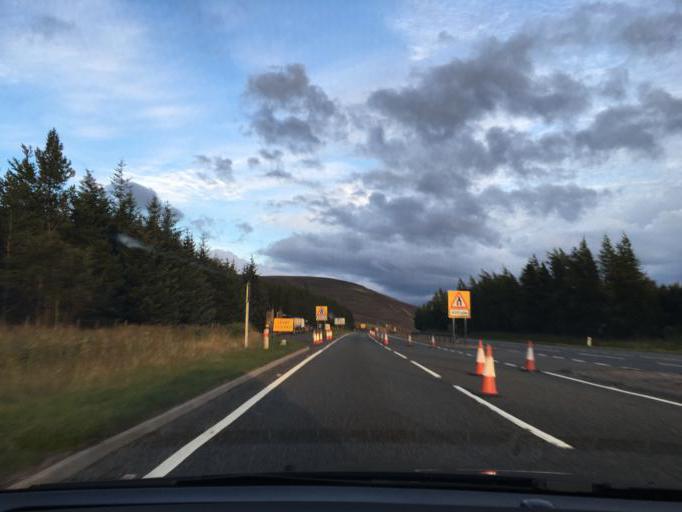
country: GB
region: Scotland
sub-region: Highland
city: Aviemore
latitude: 57.3119
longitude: -3.9489
